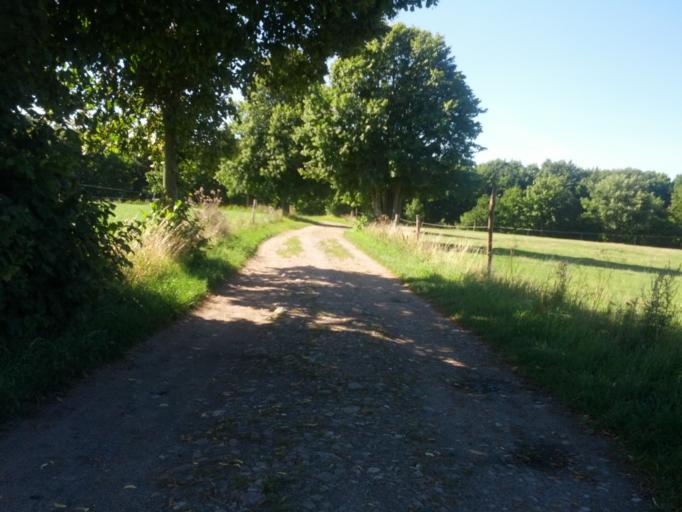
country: DE
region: Mecklenburg-Vorpommern
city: Bastorf
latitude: 54.1083
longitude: 11.6700
